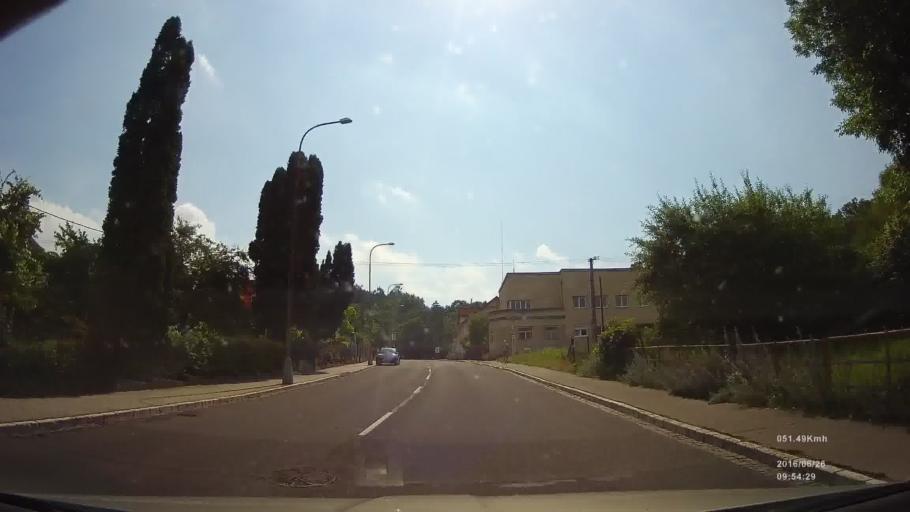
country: SK
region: Banskobystricky
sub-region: Okres Banska Bystrica
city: Zvolen
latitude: 48.6108
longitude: 19.1529
